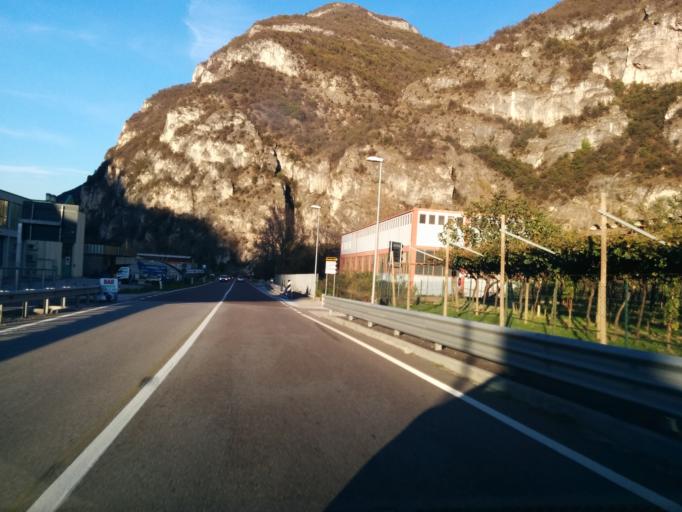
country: IT
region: Trentino-Alto Adige
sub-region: Provincia di Trento
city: Besenello
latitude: 45.9502
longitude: 11.1071
